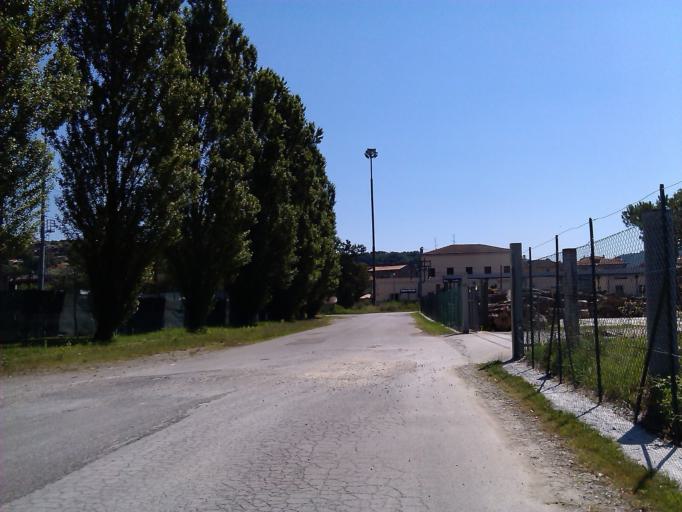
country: IT
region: Umbria
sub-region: Provincia di Terni
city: Fabro Scalo
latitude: 42.8748
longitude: 12.0398
